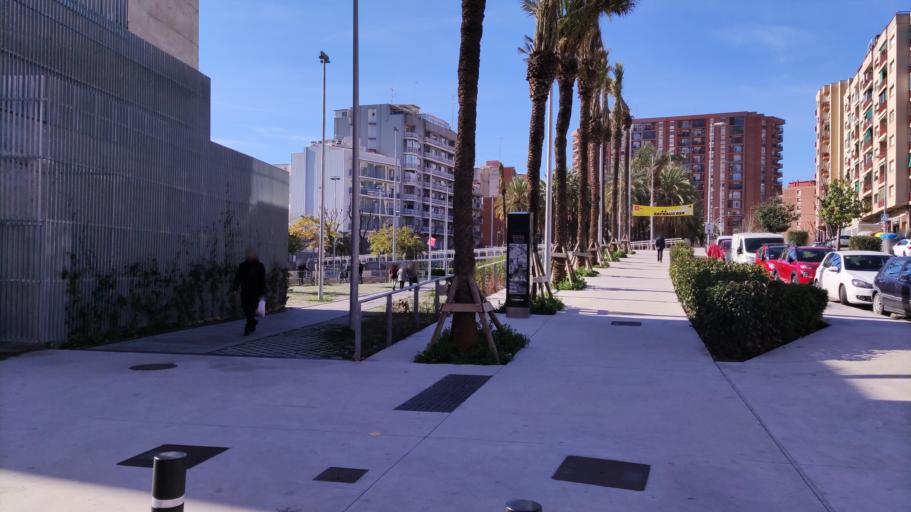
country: ES
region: Catalonia
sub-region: Provincia de Barcelona
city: Llefia
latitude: 41.4381
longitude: 2.2199
